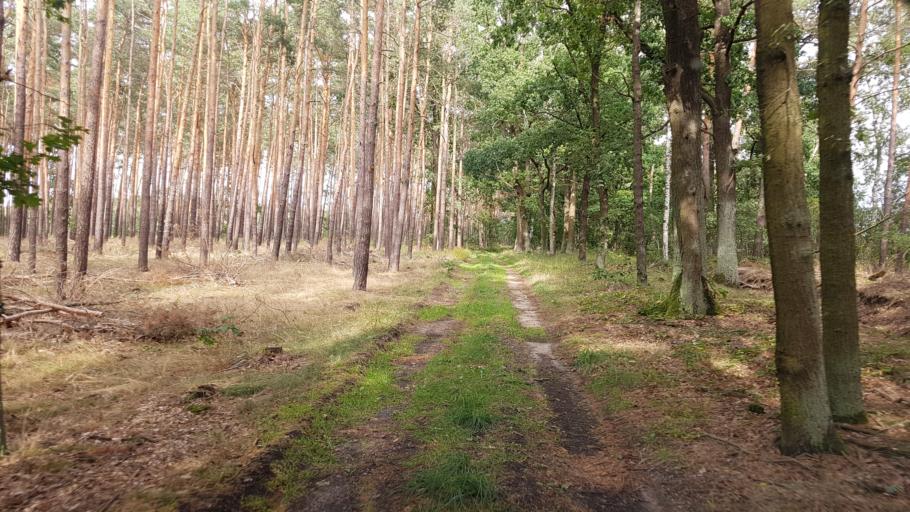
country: DE
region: Brandenburg
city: Doberlug-Kirchhain
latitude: 51.6360
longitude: 13.5952
